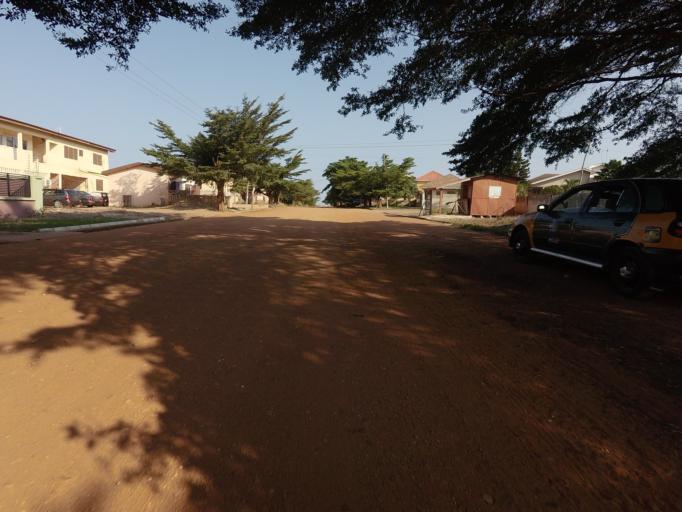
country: GH
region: Greater Accra
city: Nungua
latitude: 5.6388
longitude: -0.0861
